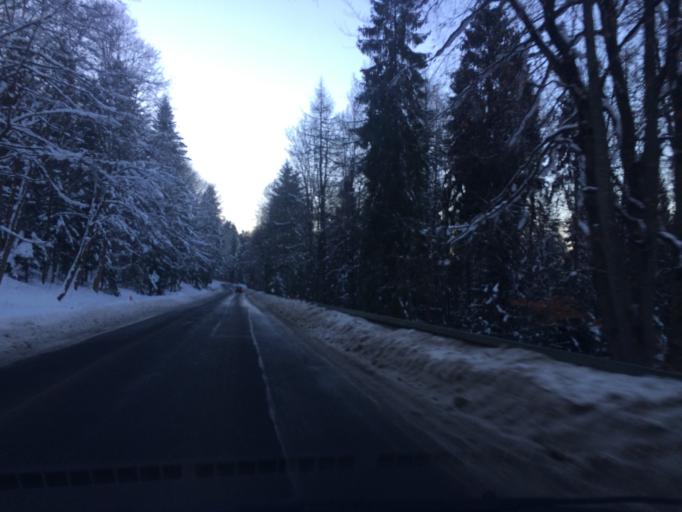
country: PL
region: Subcarpathian Voivodeship
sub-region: Powiat bieszczadzki
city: Lutowiska
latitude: 49.2869
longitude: 22.6801
